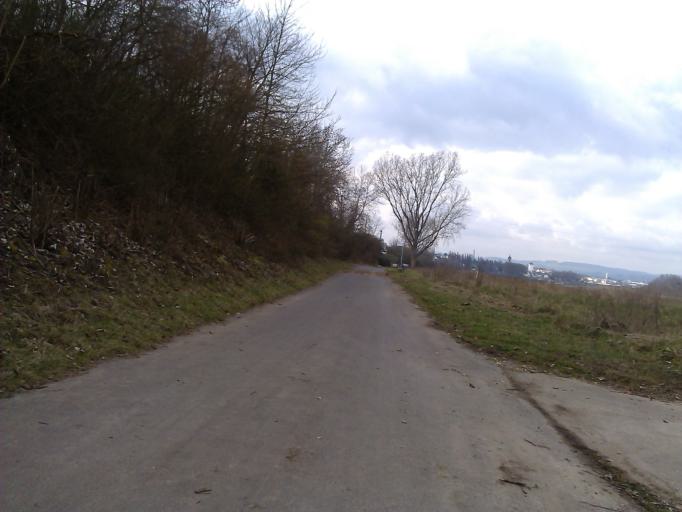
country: DE
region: Rheinland-Pfalz
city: Kettig
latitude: 50.4102
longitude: 7.4823
